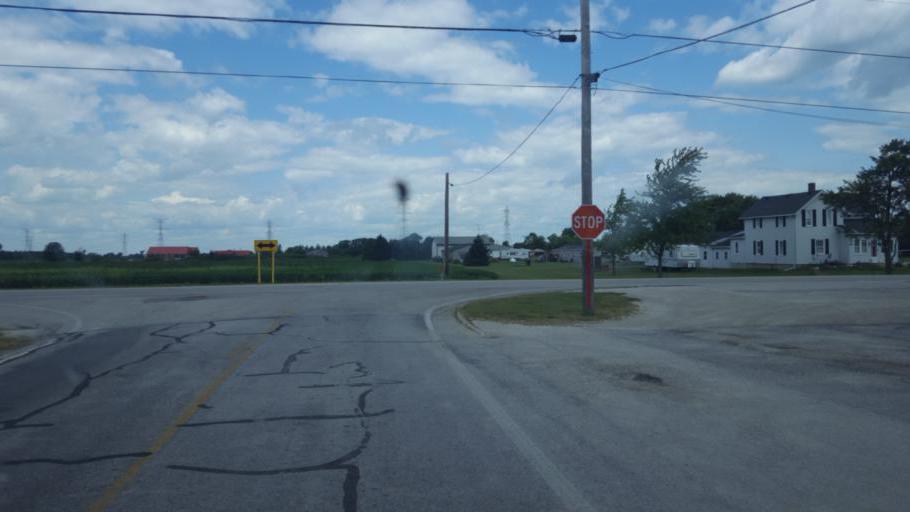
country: US
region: Ohio
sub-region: Lucas County
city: Curtice
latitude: 41.6035
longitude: -83.2804
